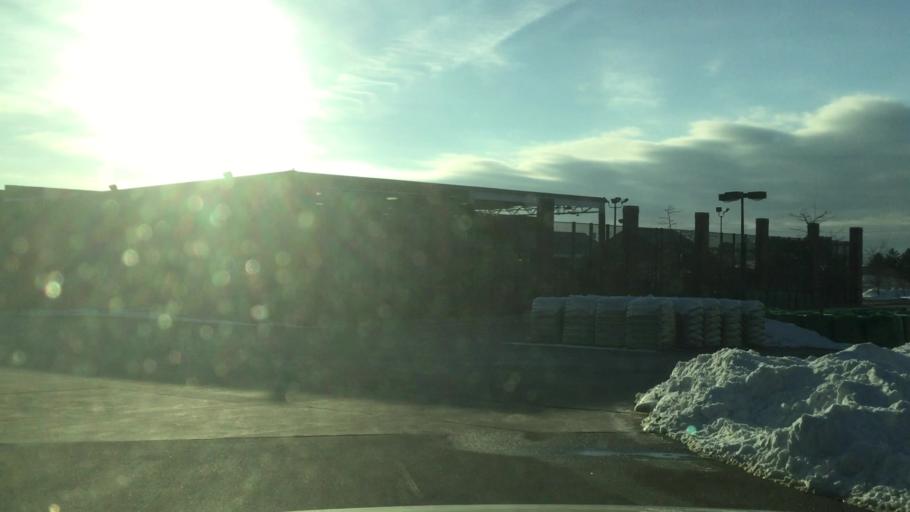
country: US
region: Michigan
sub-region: Oakland County
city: Sylvan Lake
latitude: 42.6161
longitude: -83.3096
